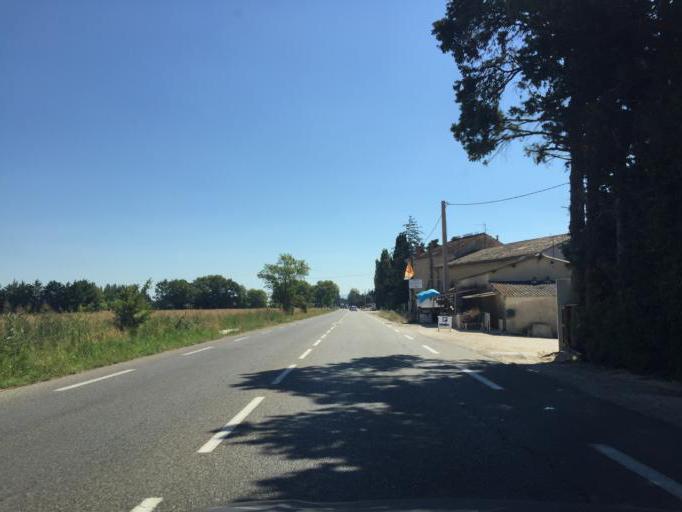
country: FR
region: Provence-Alpes-Cote d'Azur
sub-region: Departement du Vaucluse
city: L'Isle-sur-la-Sorgue
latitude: 43.8798
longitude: 5.0183
